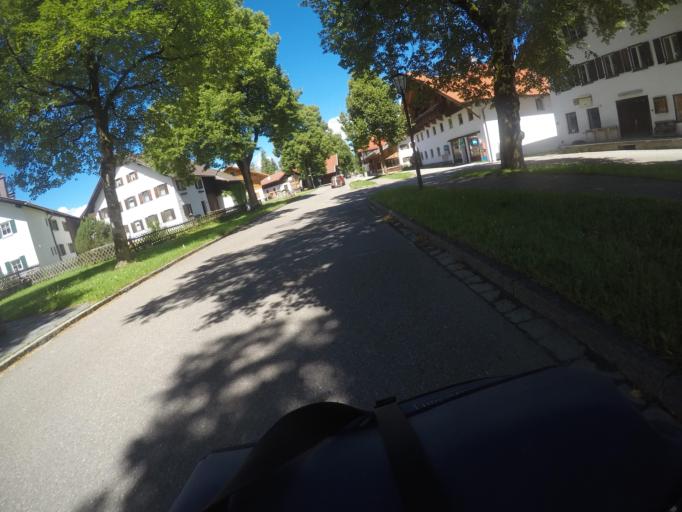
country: DE
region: Bavaria
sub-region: Swabia
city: Schwangau
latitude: 47.5799
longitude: 10.7353
